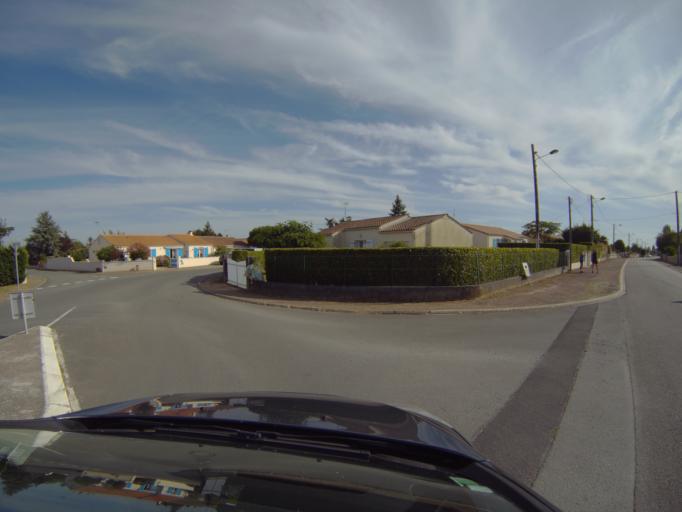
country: FR
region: Pays de la Loire
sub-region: Departement de la Vendee
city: Angles
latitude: 46.4114
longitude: -1.3949
